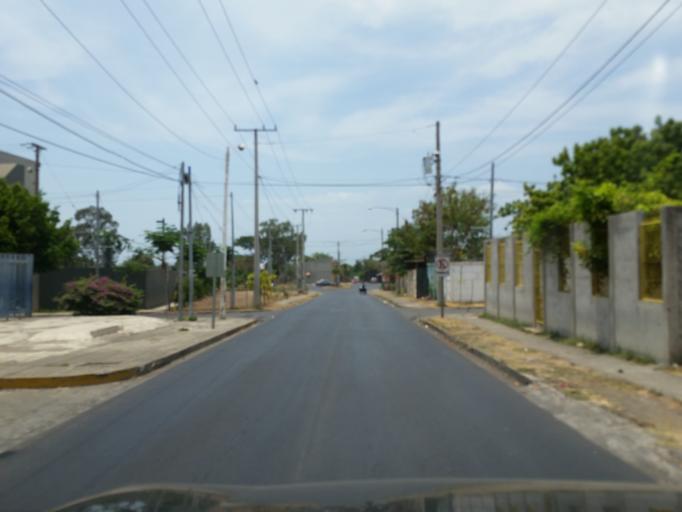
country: NI
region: Managua
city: Managua
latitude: 12.1525
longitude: -86.2680
